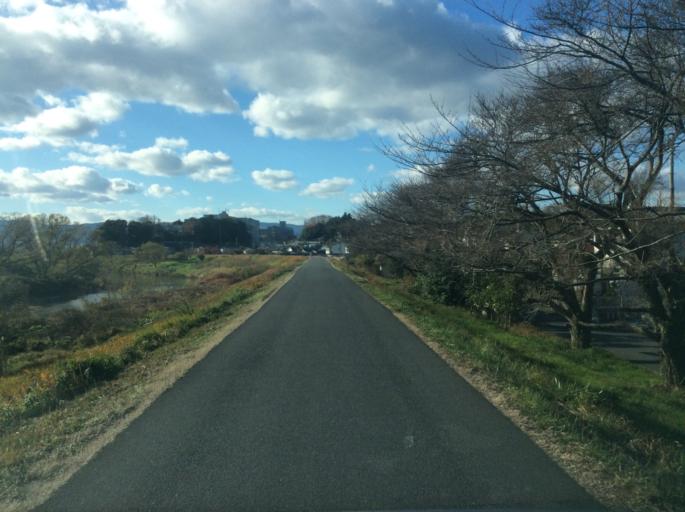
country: JP
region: Fukushima
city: Iwaki
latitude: 37.0569
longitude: 140.9158
